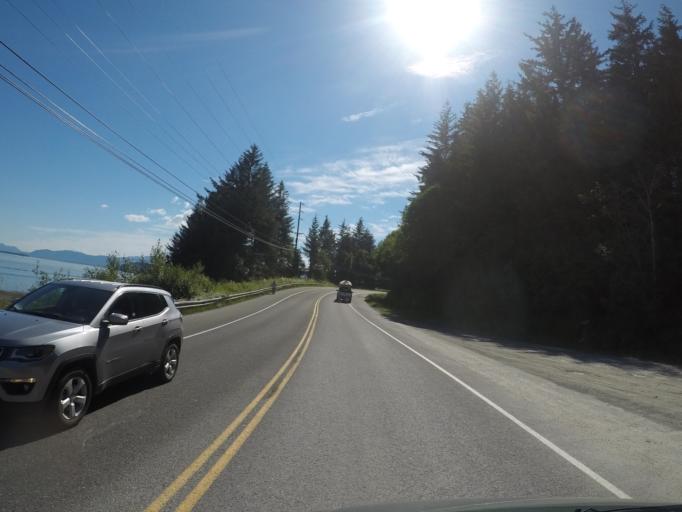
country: US
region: Alaska
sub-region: Juneau City and Borough
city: Juneau
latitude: 58.3827
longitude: -134.6686
